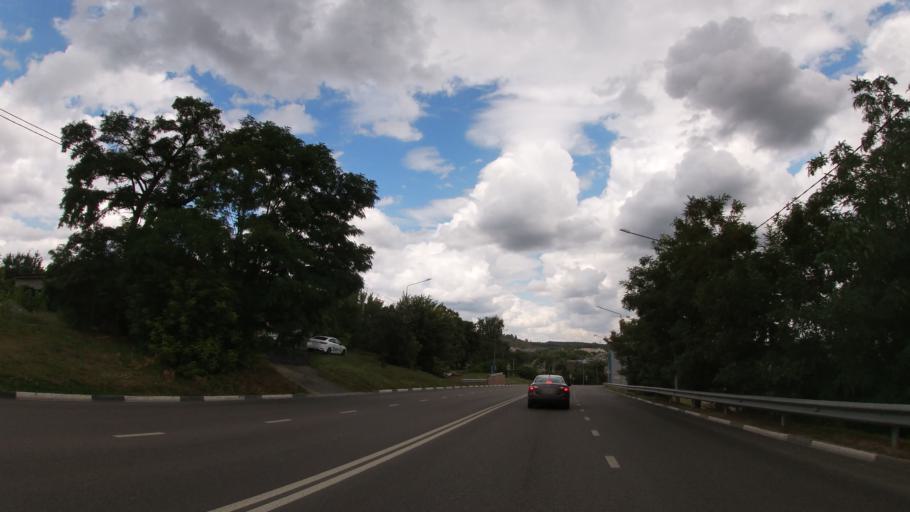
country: RU
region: Belgorod
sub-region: Belgorodskiy Rayon
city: Belgorod
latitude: 50.6042
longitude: 36.6105
